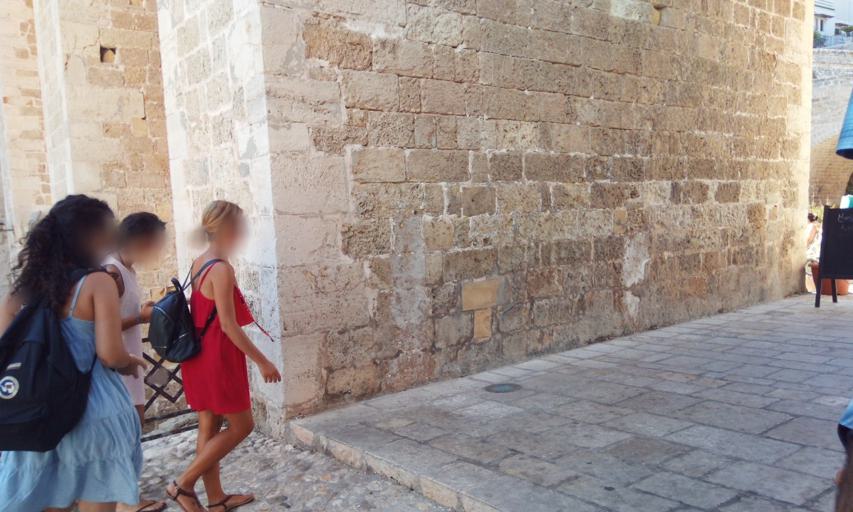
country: IT
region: Apulia
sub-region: Provincia di Bari
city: Polignano a Mare
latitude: 40.9957
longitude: 17.2179
